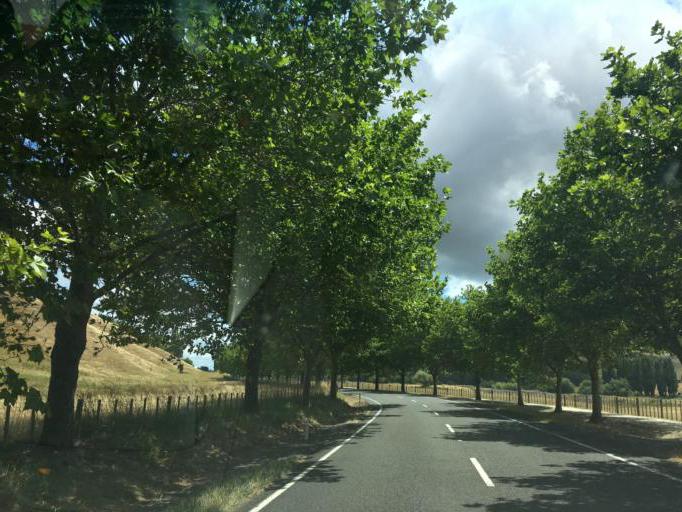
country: NZ
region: Hawke's Bay
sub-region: Hastings District
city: Hastings
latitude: -39.7070
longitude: 176.9317
